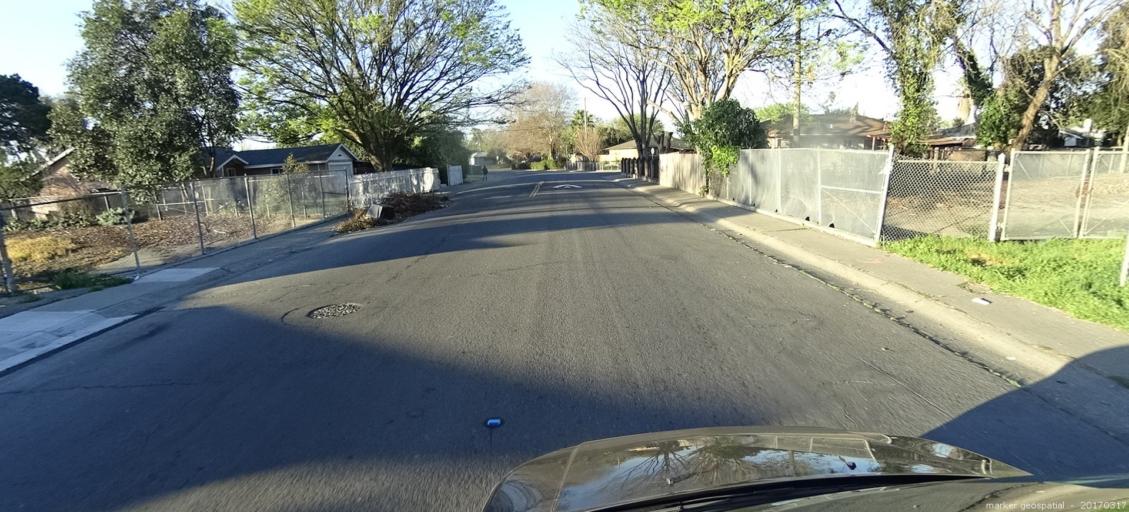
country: US
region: California
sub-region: Sacramento County
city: Parkway
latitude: 38.4944
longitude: -121.4860
